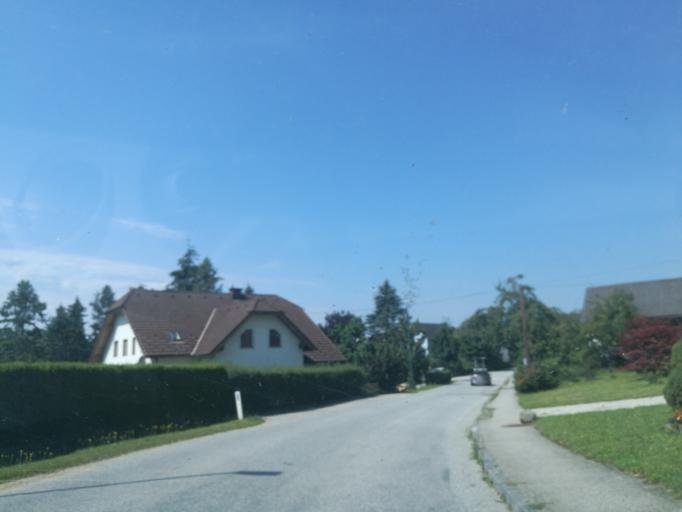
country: AT
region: Lower Austria
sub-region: Politischer Bezirk Gmund
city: Litschau
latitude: 48.9453
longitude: 15.0861
